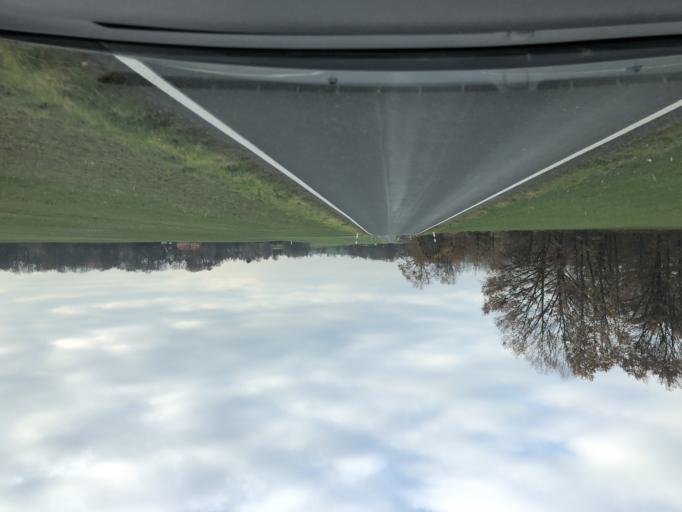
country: DE
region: Saxony
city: Mutzschen
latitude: 51.2824
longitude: 12.8701
